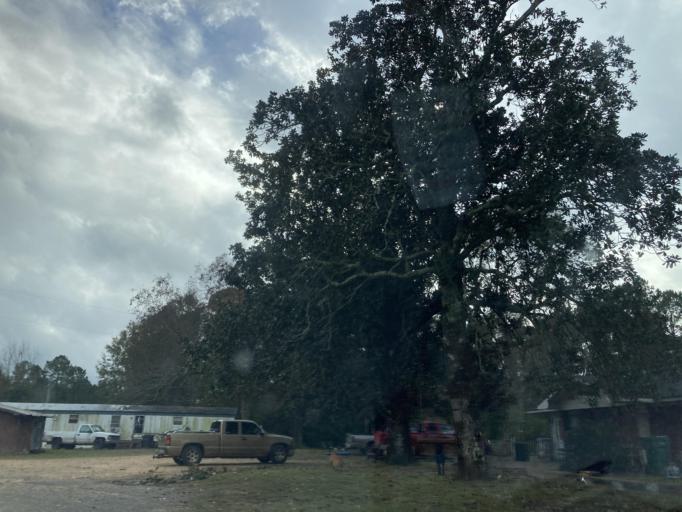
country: US
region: Mississippi
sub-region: Lamar County
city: Purvis
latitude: 31.1494
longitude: -89.5512
